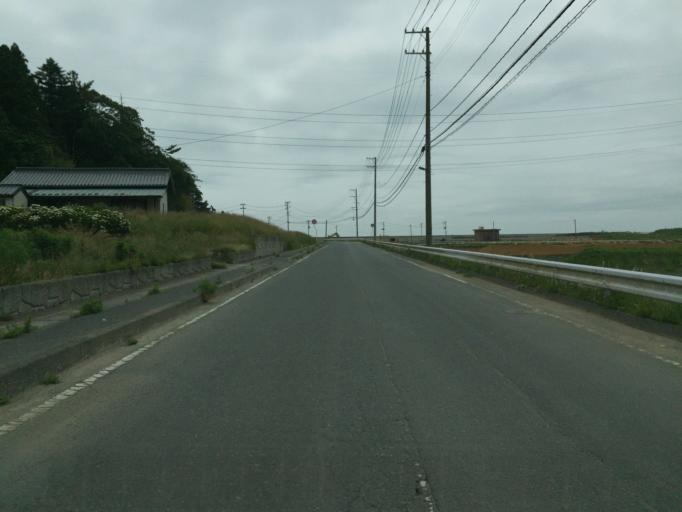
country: JP
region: Fukushima
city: Namie
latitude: 37.6630
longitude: 141.0123
